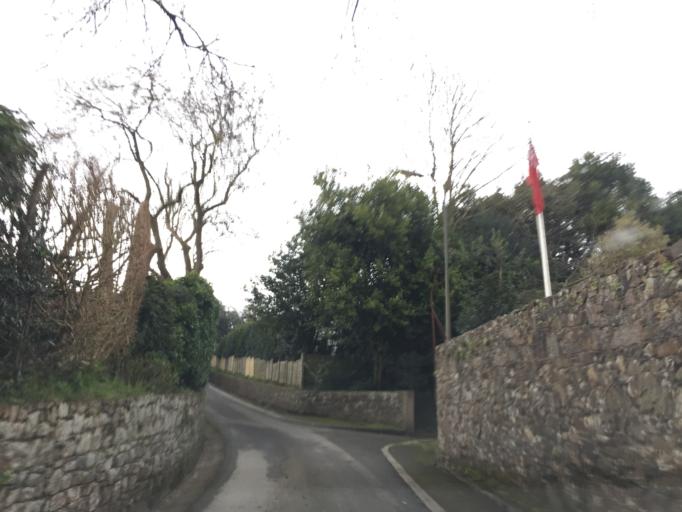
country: JE
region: St Helier
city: Saint Helier
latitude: 49.1971
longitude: -2.0914
